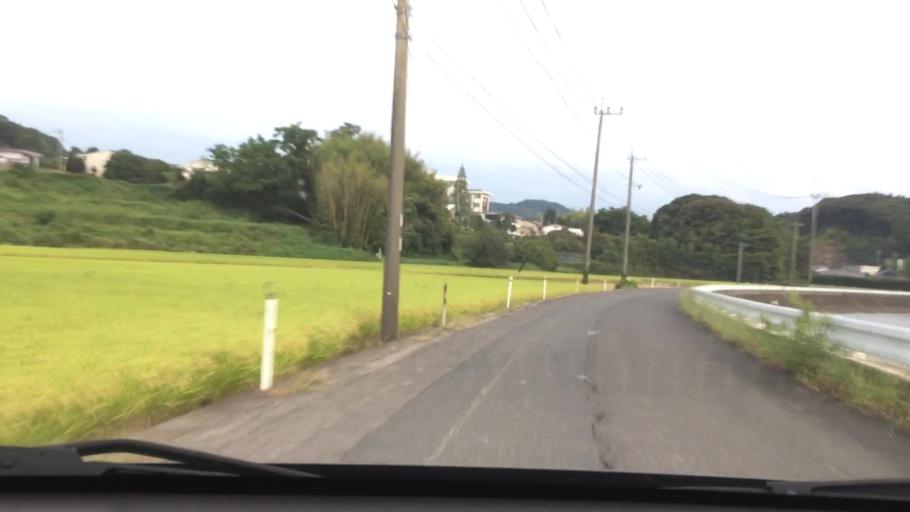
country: JP
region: Nagasaki
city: Togitsu
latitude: 32.9907
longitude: 129.7728
